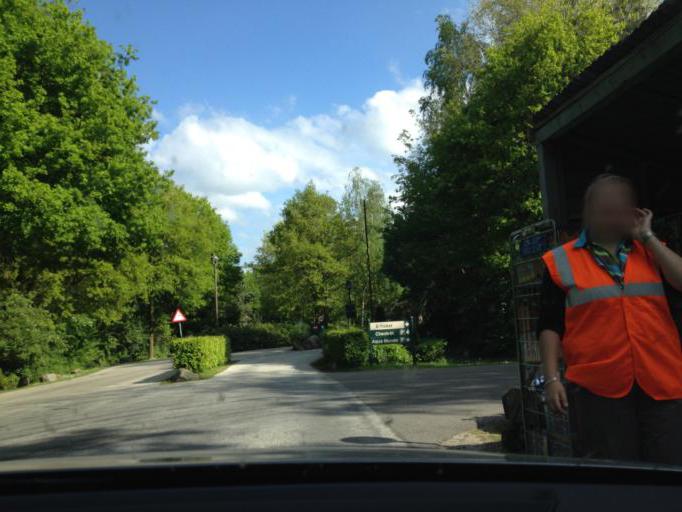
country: NL
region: Utrecht
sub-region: Gemeente Bunschoten
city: Bunschoten
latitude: 52.2630
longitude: 5.3962
